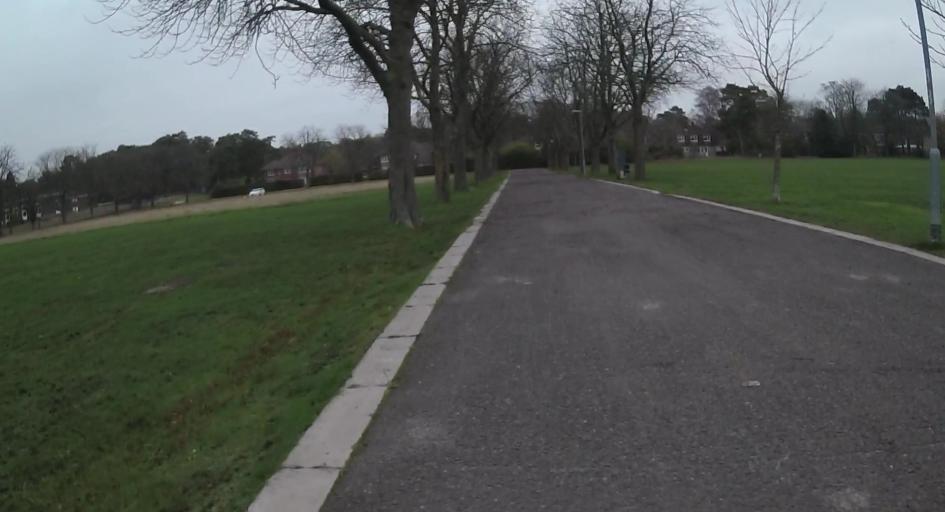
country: GB
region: England
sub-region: Surrey
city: Bagshot
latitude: 51.3153
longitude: -0.6952
